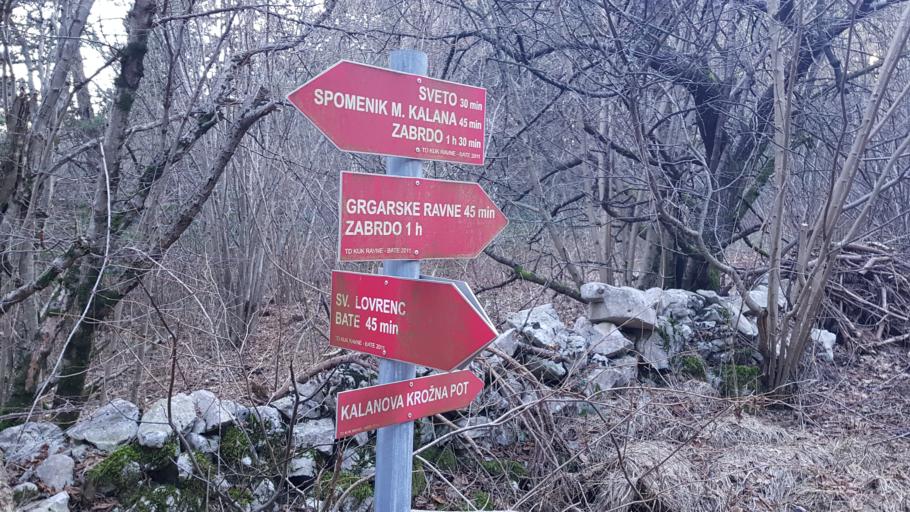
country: SI
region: Kanal
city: Kanal
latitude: 46.0338
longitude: 13.6847
